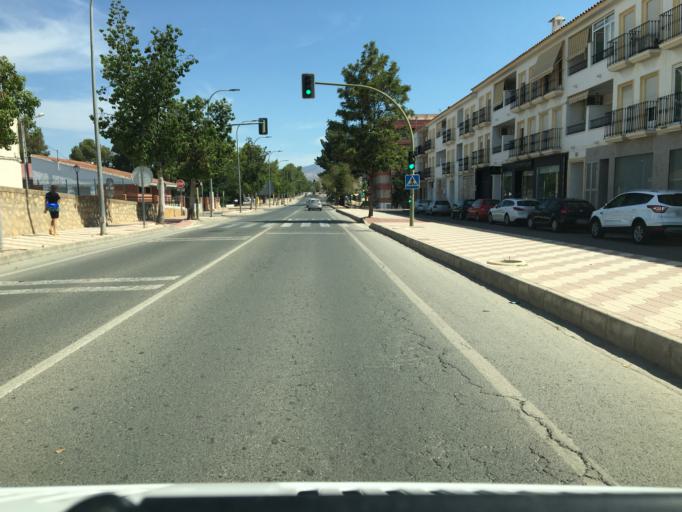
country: ES
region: Andalusia
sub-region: Provincia de Almeria
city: Huercal-Overa
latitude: 37.3982
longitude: -1.9394
